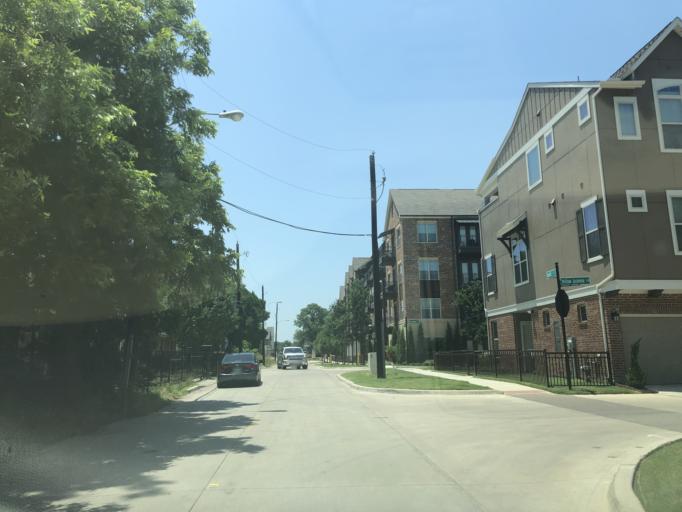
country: US
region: Texas
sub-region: Dallas County
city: Dallas
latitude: 32.7764
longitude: -96.8404
